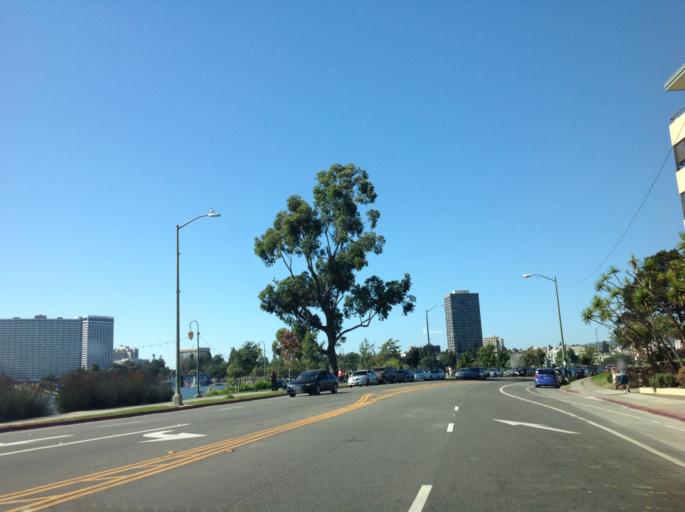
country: US
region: California
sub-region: Alameda County
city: Oakland
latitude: 37.8011
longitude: -122.2542
